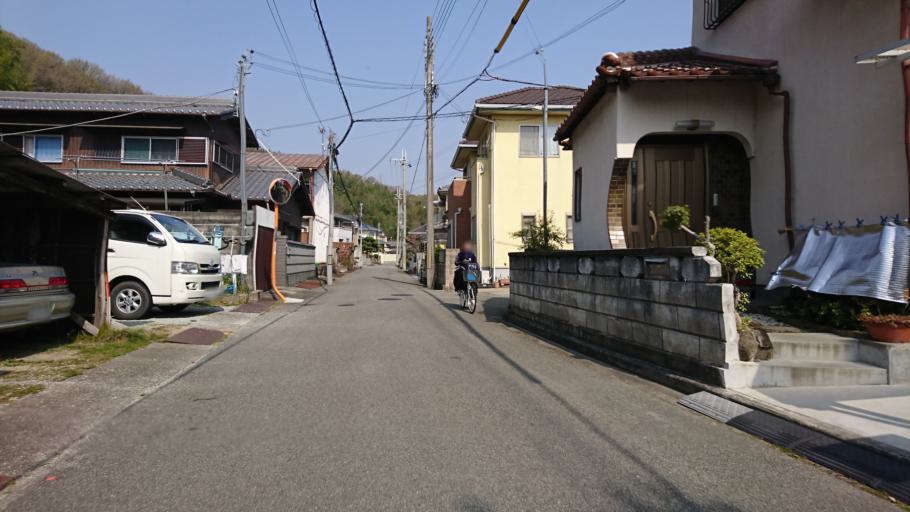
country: JP
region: Hyogo
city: Shirahamacho-usazakiminami
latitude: 34.7834
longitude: 134.7683
